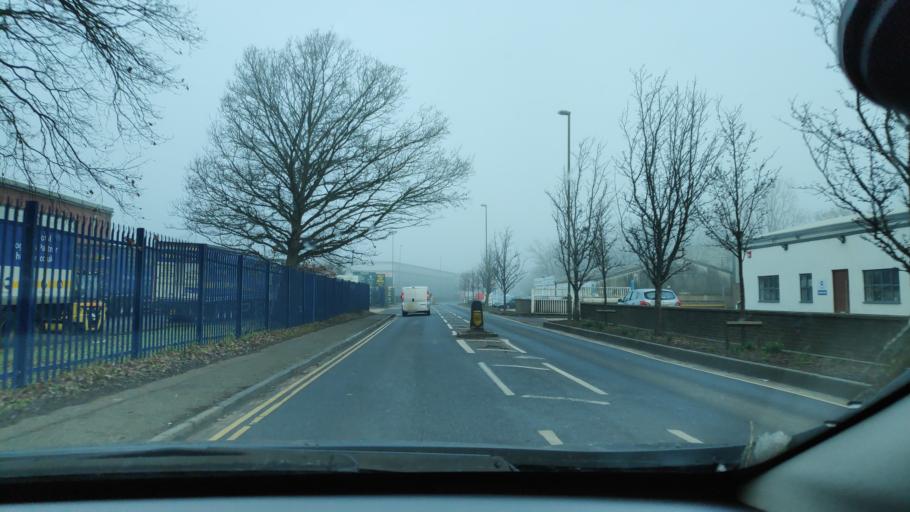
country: GB
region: England
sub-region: Hampshire
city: Farnborough
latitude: 51.2737
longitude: -0.7262
